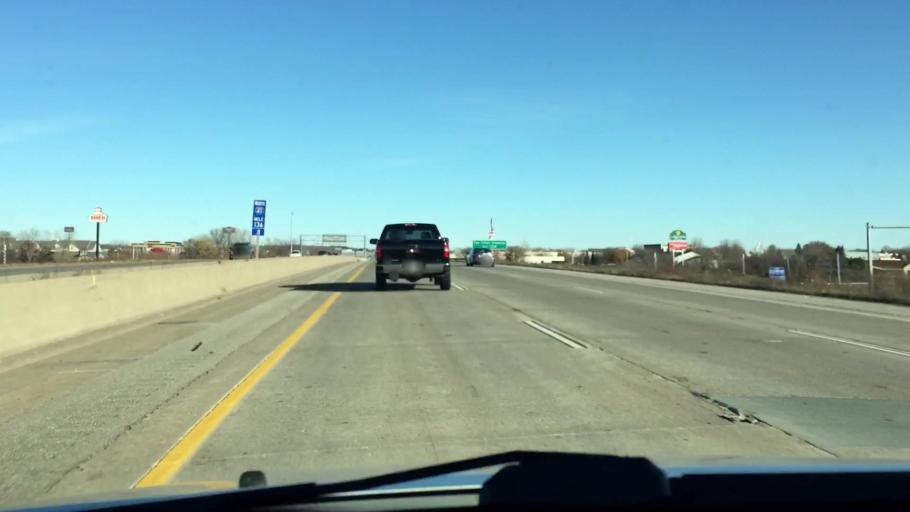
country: US
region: Wisconsin
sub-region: Outagamie County
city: Appleton
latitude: 44.2598
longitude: -88.4663
